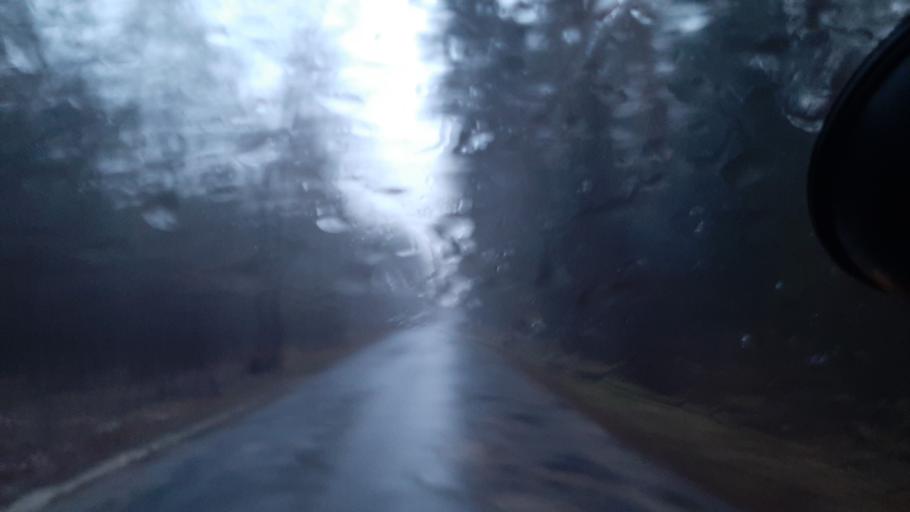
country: PL
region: Lublin Voivodeship
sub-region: Powiat lubartowski
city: Firlej
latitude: 51.5463
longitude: 22.5057
